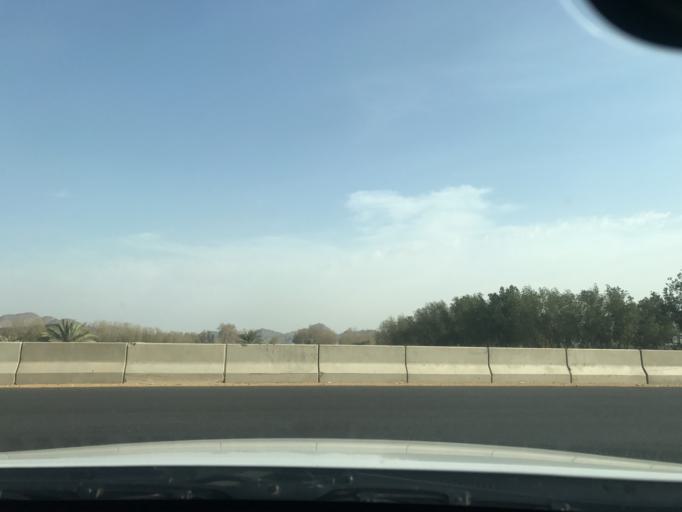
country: SA
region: Makkah
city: Al Jumum
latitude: 21.4415
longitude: 39.5357
